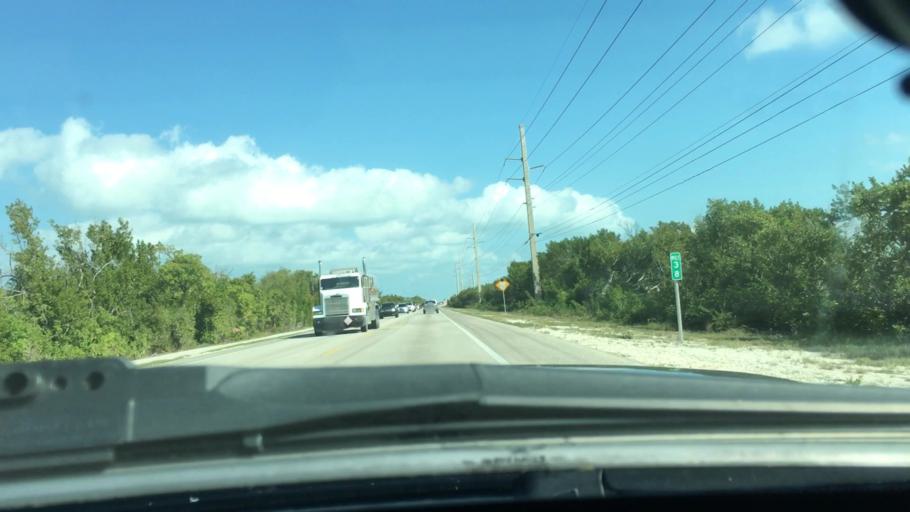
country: US
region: Florida
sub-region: Monroe County
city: Big Pine Key
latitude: 24.6672
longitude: -81.2574
